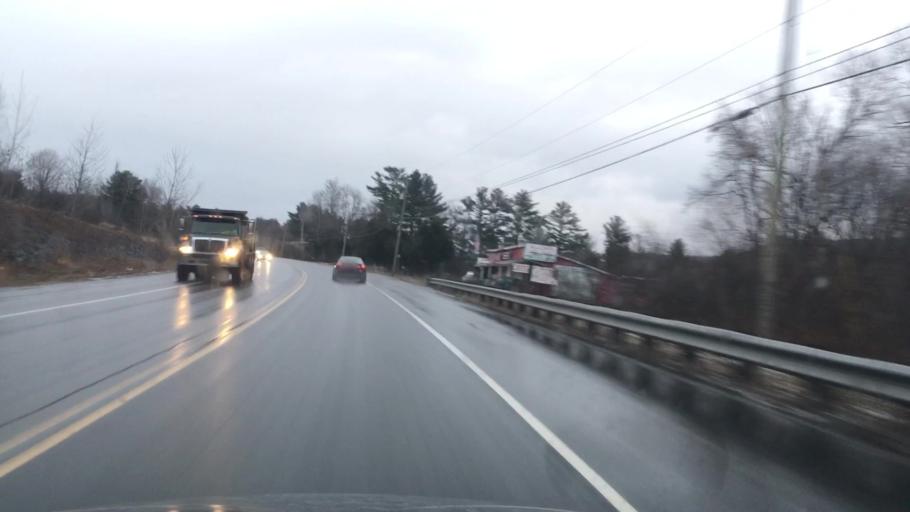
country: US
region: New Hampshire
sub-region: Sullivan County
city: Claremont
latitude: 43.3638
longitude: -72.2895
